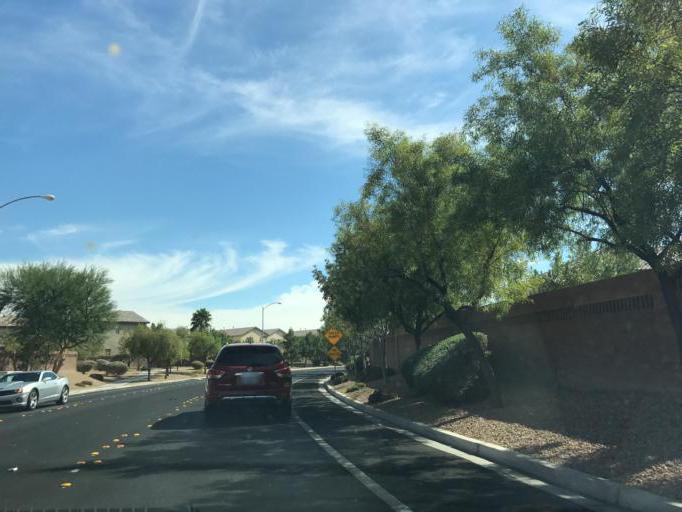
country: US
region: Nevada
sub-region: Clark County
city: Whitney
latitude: 36.1237
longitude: -115.0362
